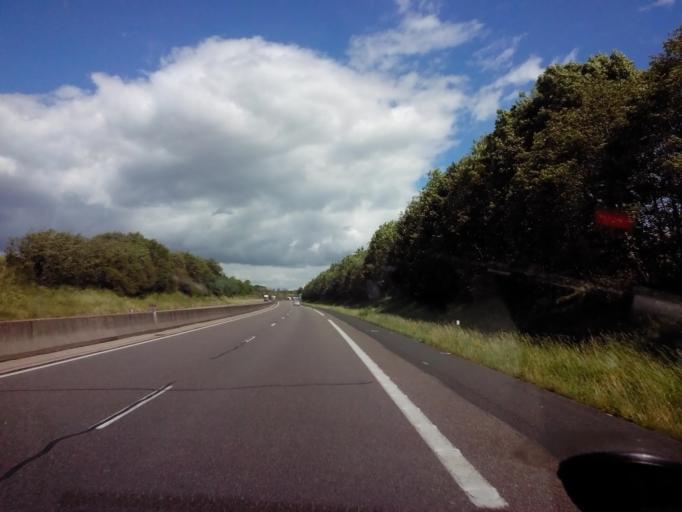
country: FR
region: Lorraine
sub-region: Departement des Vosges
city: Bulgneville
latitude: 48.2112
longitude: 5.8180
